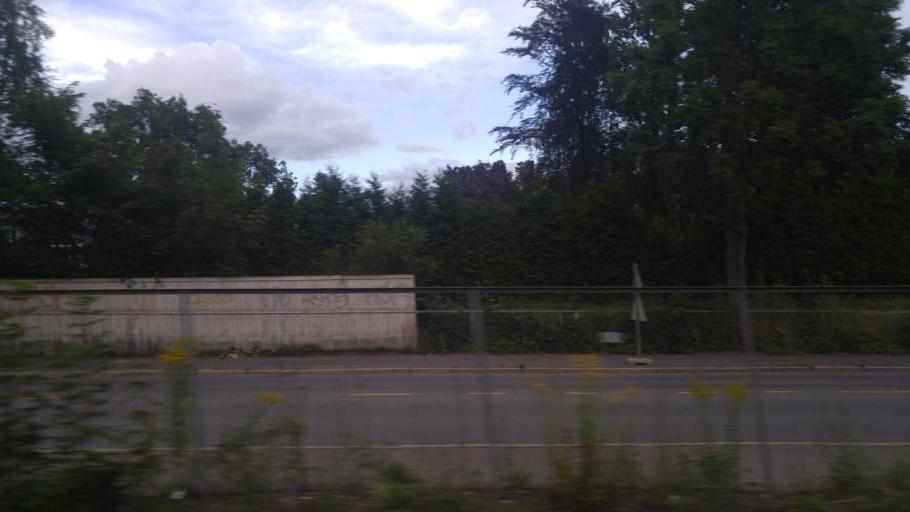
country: NO
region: Oslo
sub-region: Oslo
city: Sjolyststranda
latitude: 59.9477
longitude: 10.7055
